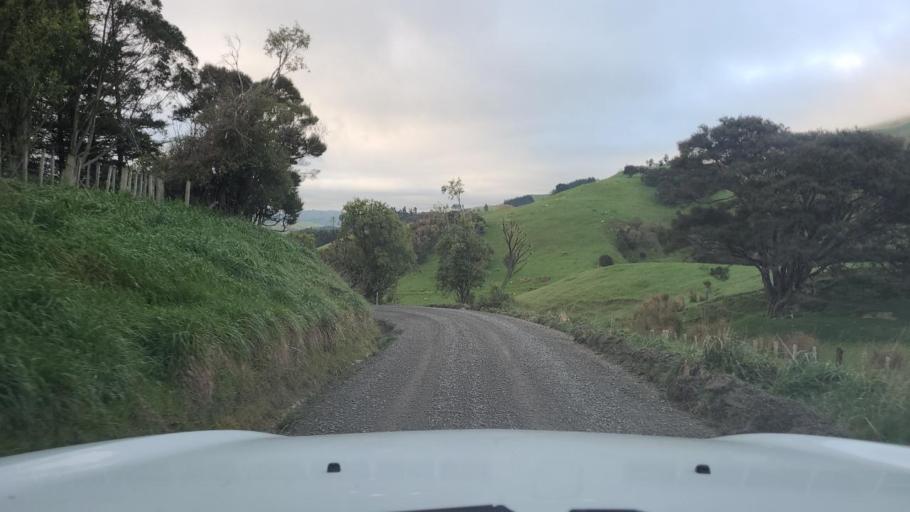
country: NZ
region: Wellington
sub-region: Masterton District
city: Masterton
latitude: -41.1615
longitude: 175.6844
